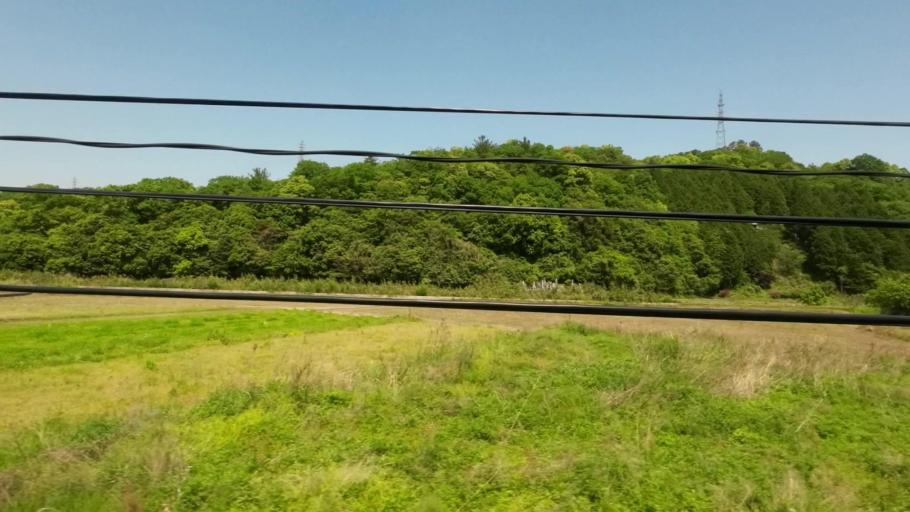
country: JP
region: Ehime
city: Niihama
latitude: 33.9333
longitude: 133.2727
